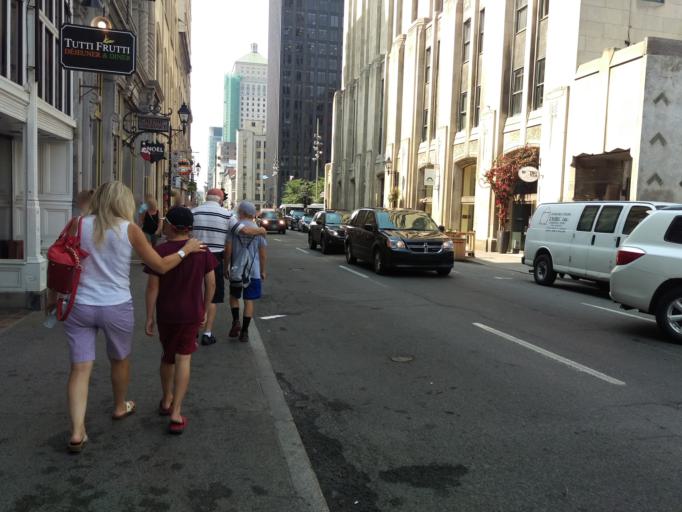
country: CA
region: Quebec
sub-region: Montreal
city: Montreal
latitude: 45.5055
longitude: -73.5563
